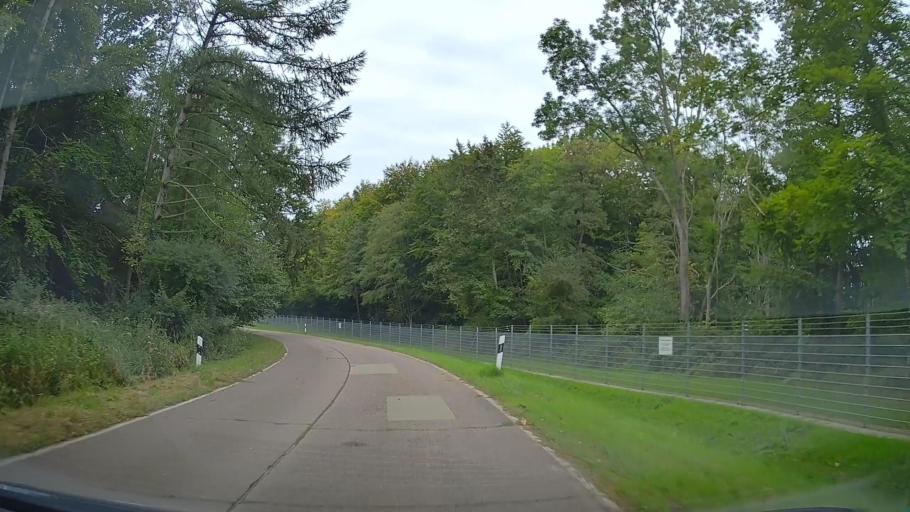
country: DE
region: Schleswig-Holstein
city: Panker
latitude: 54.3637
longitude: 10.5714
